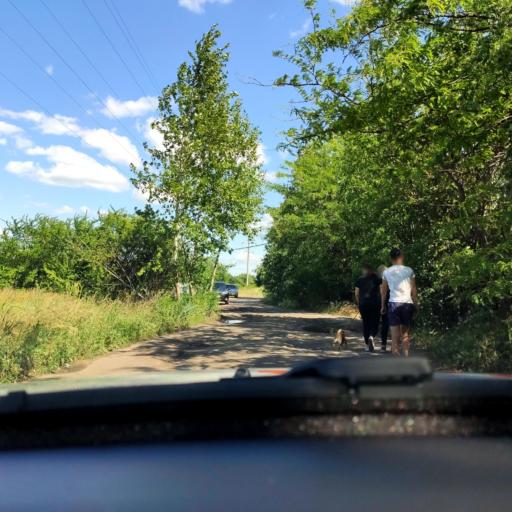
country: RU
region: Voronezj
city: Shilovo
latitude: 51.5187
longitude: 39.1526
